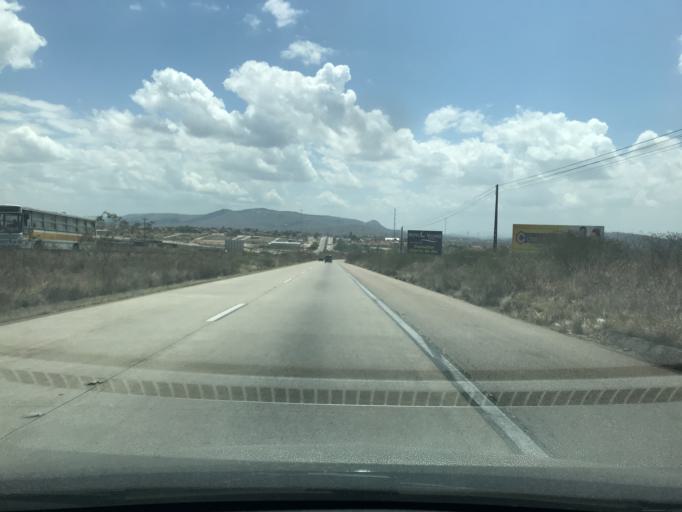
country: BR
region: Pernambuco
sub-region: Bezerros
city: Bezerros
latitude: -8.2975
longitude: -35.8326
